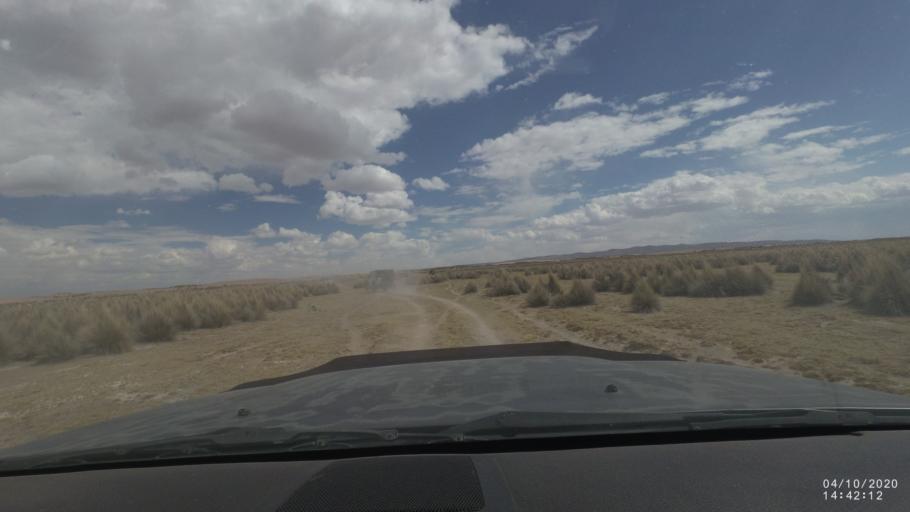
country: BO
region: Oruro
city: Poopo
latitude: -18.6855
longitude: -67.4911
